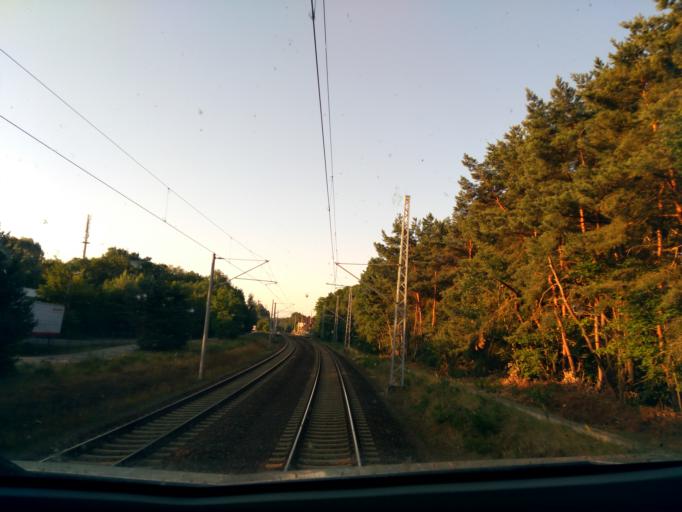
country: DE
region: Brandenburg
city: Gross Koris
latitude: 52.1625
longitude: 13.6492
